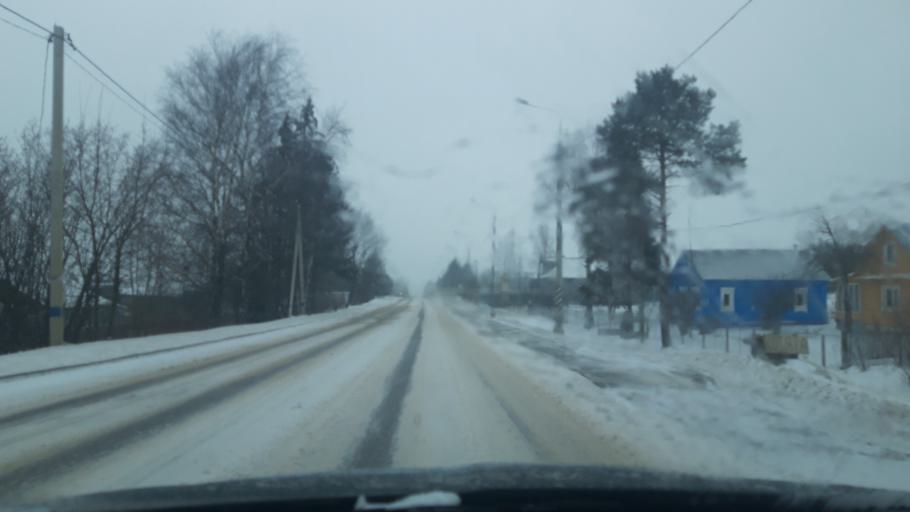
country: RU
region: Moskovskaya
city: Avtopoligon
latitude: 56.2402
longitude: 37.2458
